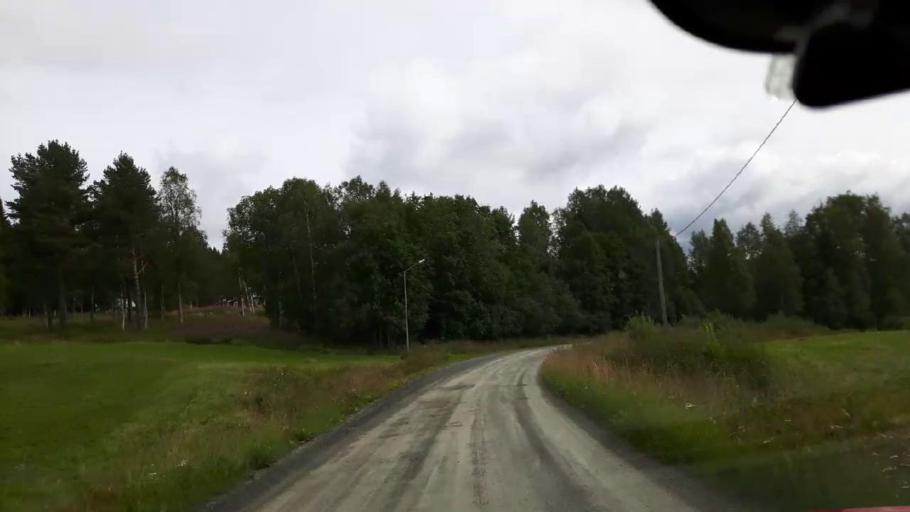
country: SE
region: Jaemtland
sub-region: Krokoms Kommun
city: Valla
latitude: 63.6739
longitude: 13.9464
